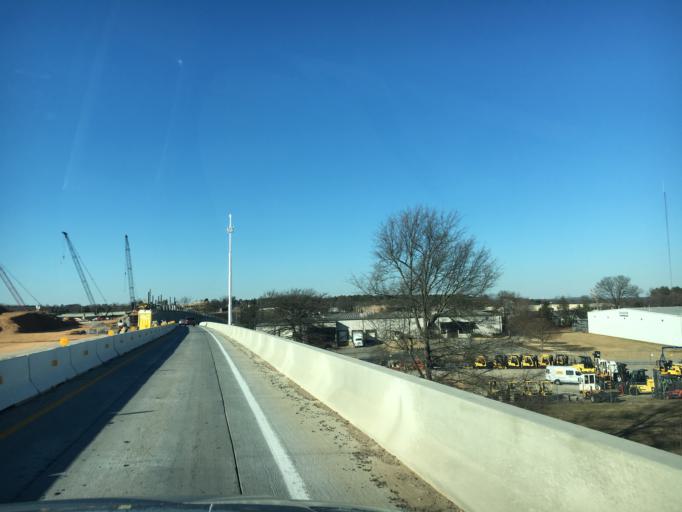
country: US
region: South Carolina
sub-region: Greenville County
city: Mauldin
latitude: 34.8301
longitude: -82.2938
